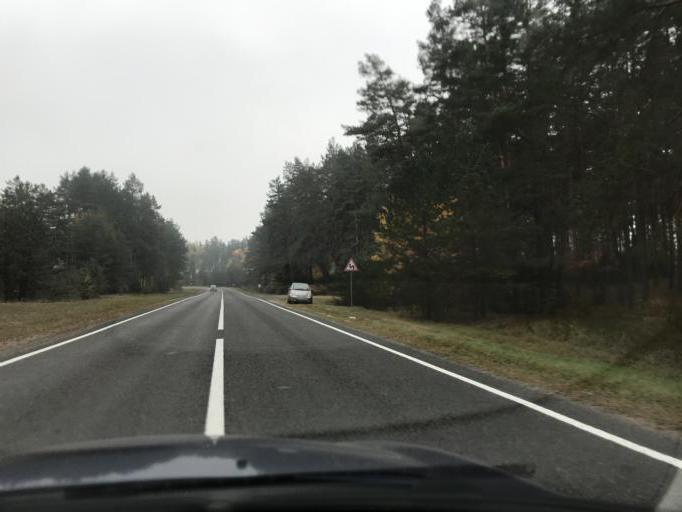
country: BY
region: Grodnenskaya
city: Hrodna
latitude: 53.8502
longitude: 23.8909
